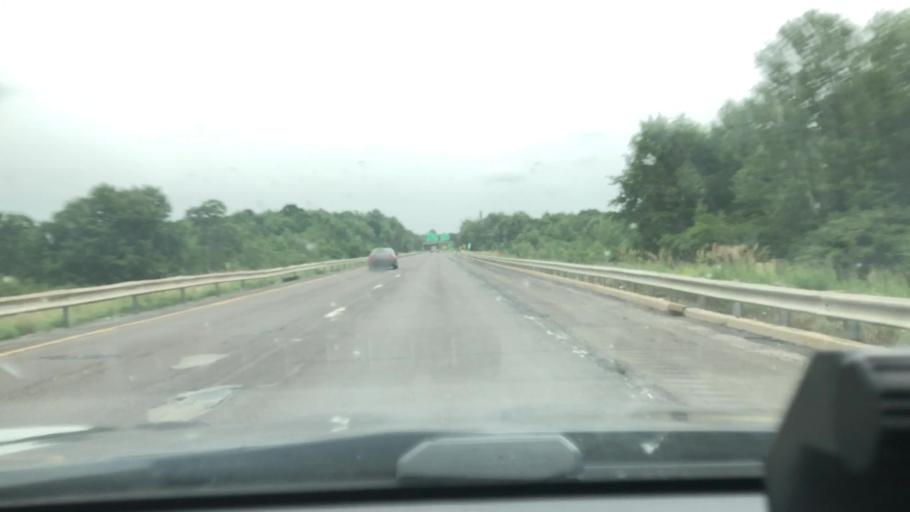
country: US
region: Pennsylvania
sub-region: Monroe County
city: Emerald Lakes
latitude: 41.0810
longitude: -75.3966
